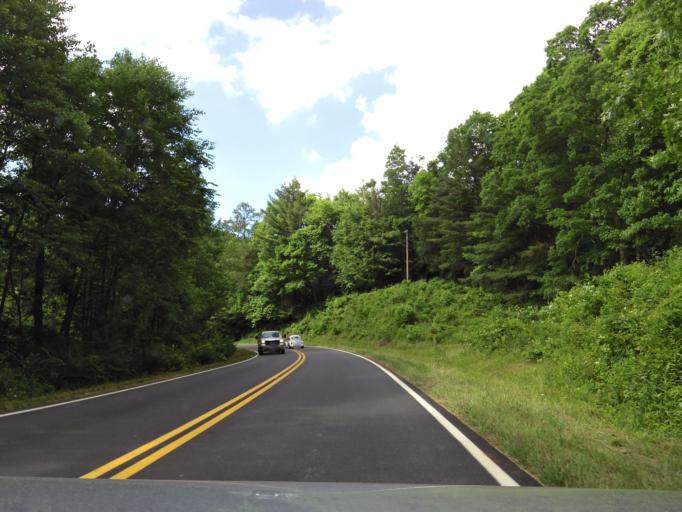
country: US
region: Georgia
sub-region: Towns County
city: Hiawassee
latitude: 34.8429
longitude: -83.7741
